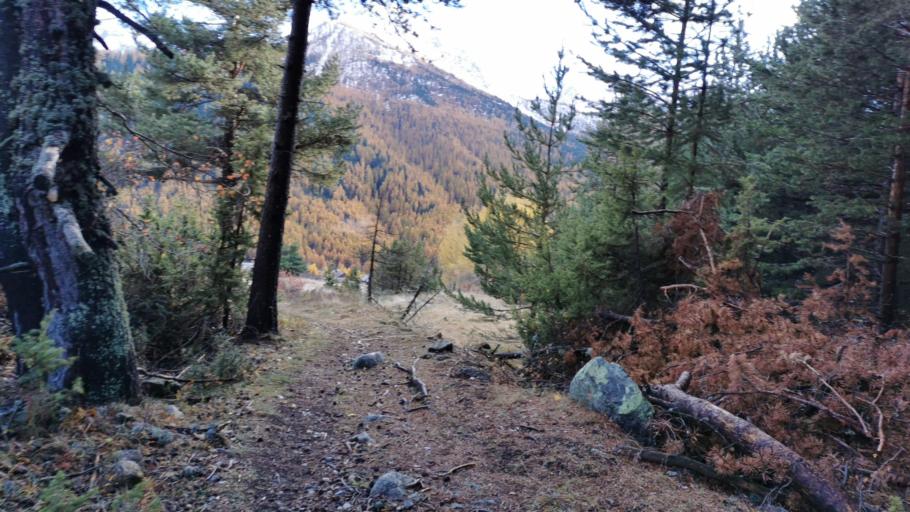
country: IT
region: Piedmont
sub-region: Provincia di Torino
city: Bardonecchia
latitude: 45.0241
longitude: 6.6331
